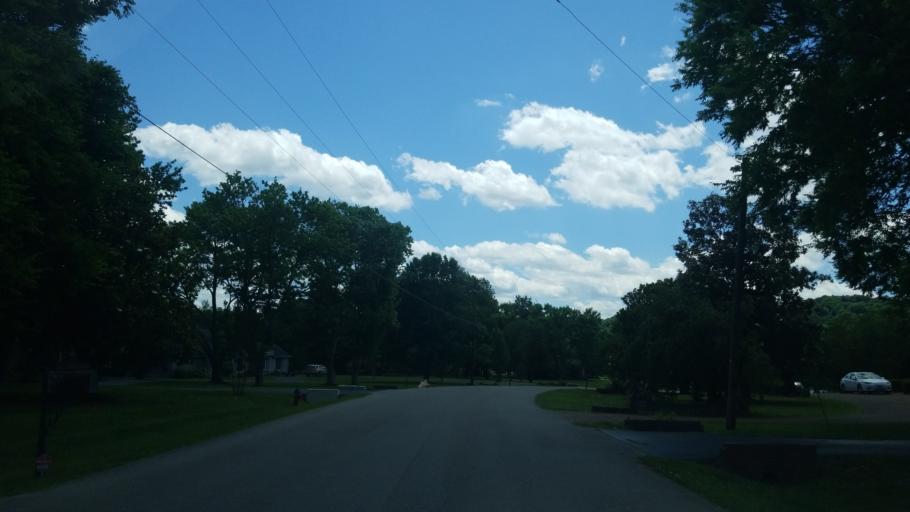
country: US
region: Tennessee
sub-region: Davidson County
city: Forest Hills
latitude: 36.0336
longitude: -86.8243
